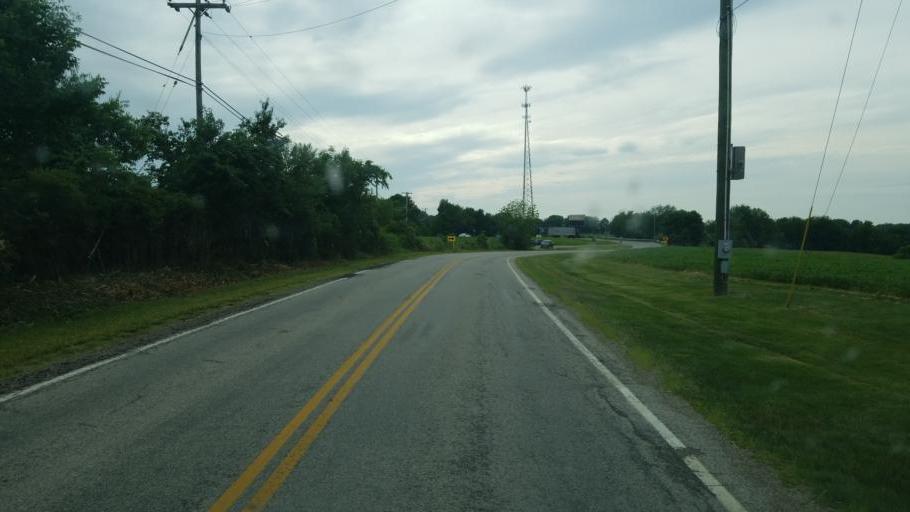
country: US
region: Ohio
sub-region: Stark County
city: Canal Fulton
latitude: 40.8905
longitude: -81.6196
